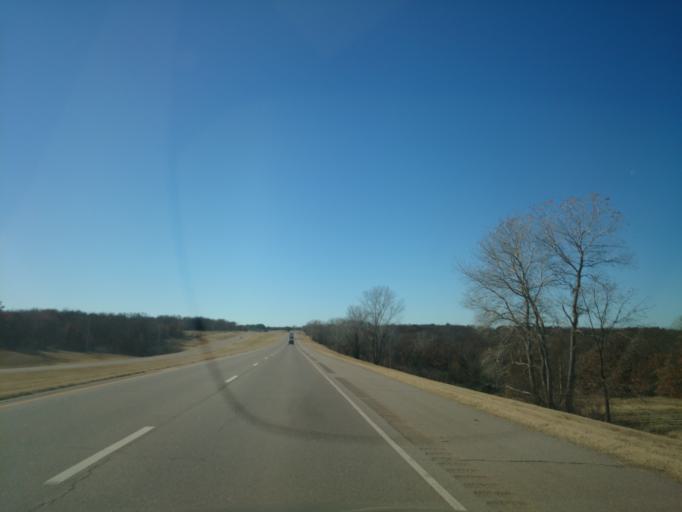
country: US
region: Oklahoma
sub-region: Payne County
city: Stillwater
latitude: 36.1102
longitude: -97.1977
